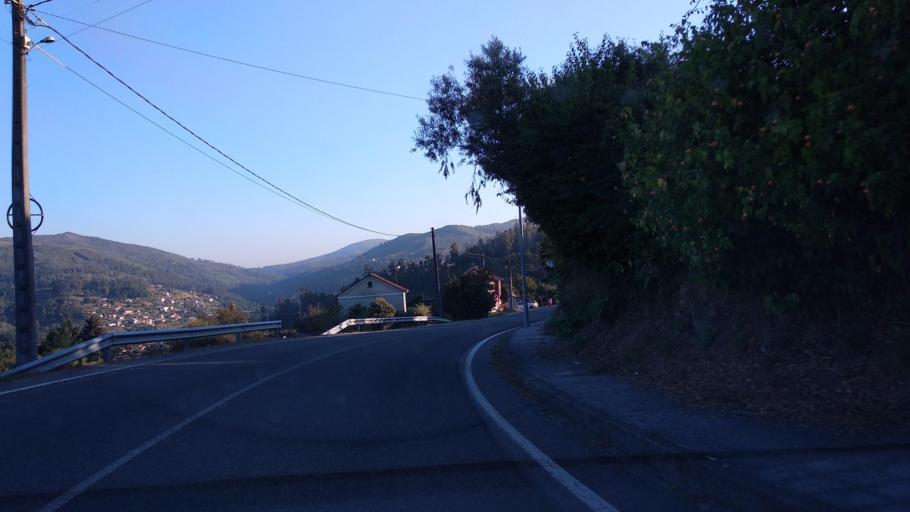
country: ES
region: Galicia
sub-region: Provincia de Pontevedra
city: Ponte Caldelas
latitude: 42.3542
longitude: -8.5425
